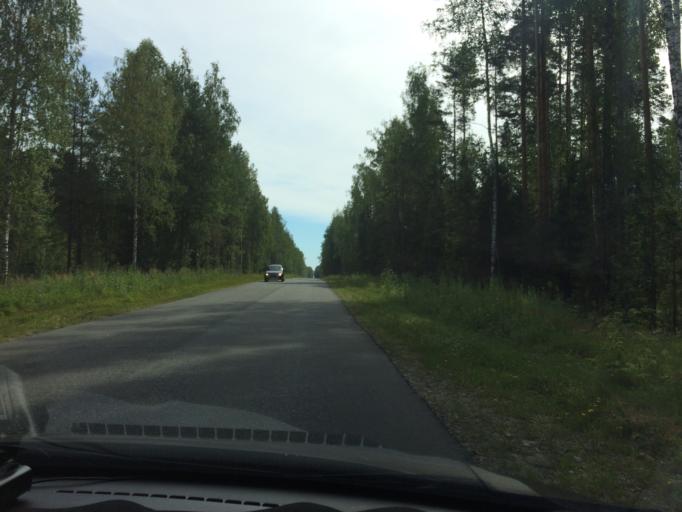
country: RU
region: Mariy-El
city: Mochalishche
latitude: 56.5480
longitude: 48.3446
